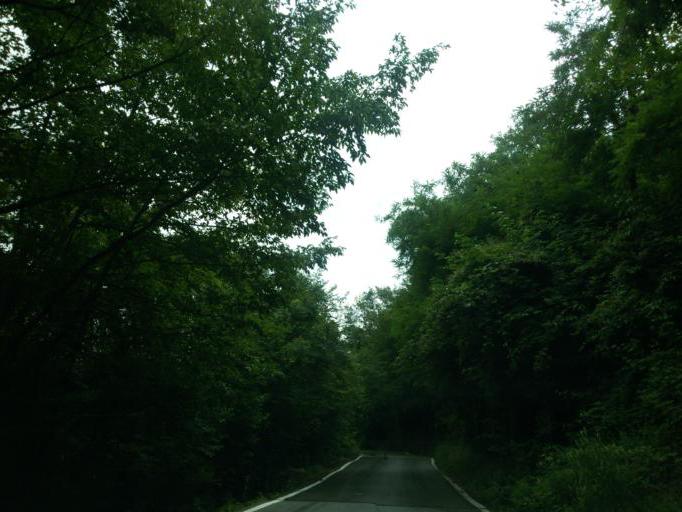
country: IT
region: Liguria
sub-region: Provincia di Genova
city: Piccarello
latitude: 44.4402
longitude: 9.0043
